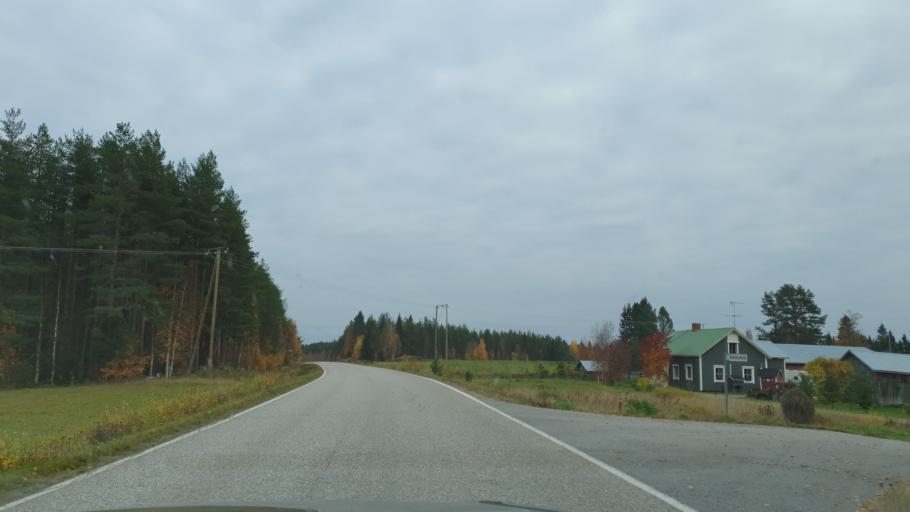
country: FI
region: Kainuu
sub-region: Kajaani
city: Ristijaervi
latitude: 64.4573
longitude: 28.3269
